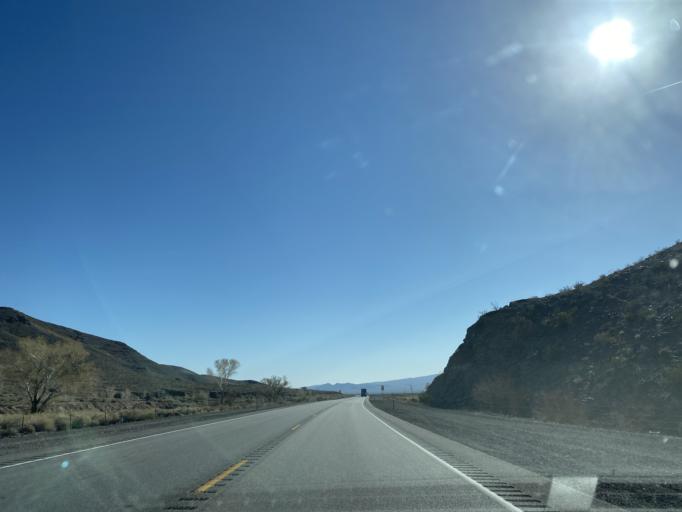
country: US
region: Nevada
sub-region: Nye County
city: Beatty
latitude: 36.8860
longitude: -116.7514
